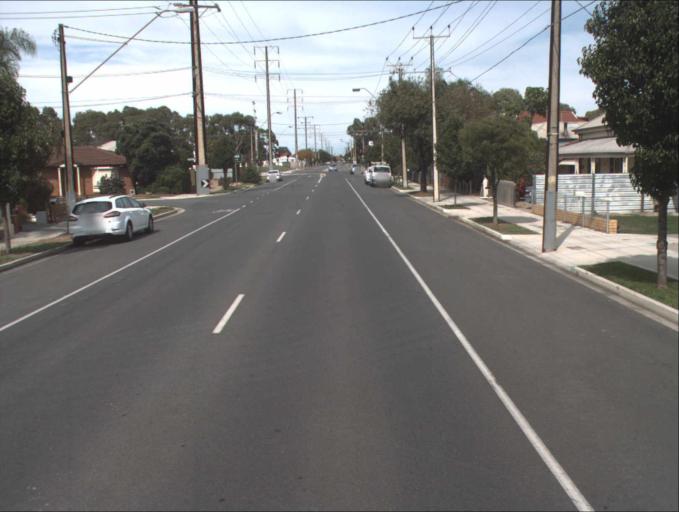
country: AU
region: South Australia
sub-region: Port Adelaide Enfield
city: Birkenhead
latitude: -34.8438
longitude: 138.4874
